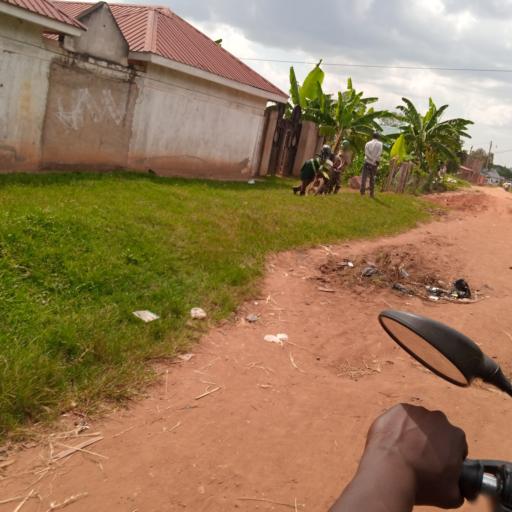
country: UG
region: Eastern Region
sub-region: Mbale District
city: Mbale
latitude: 1.1016
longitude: 34.1779
